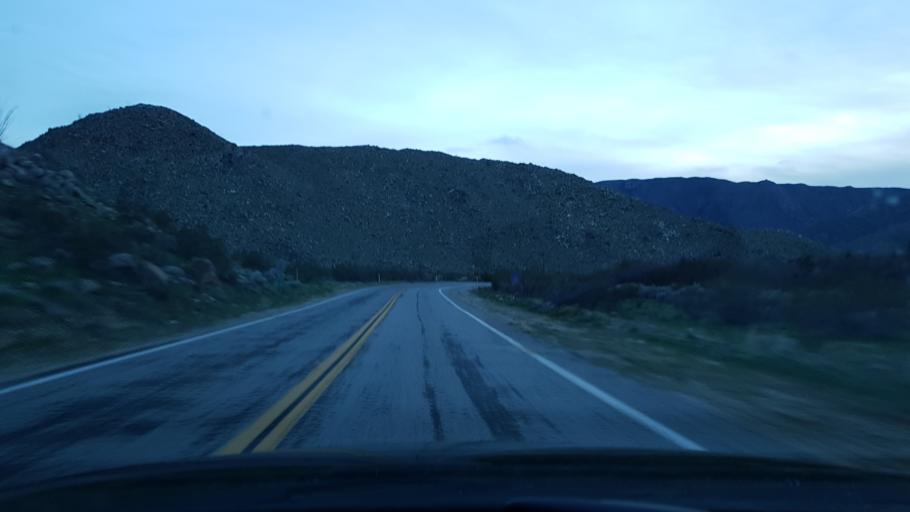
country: US
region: California
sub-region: San Diego County
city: Pine Valley
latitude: 32.9801
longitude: -116.4216
